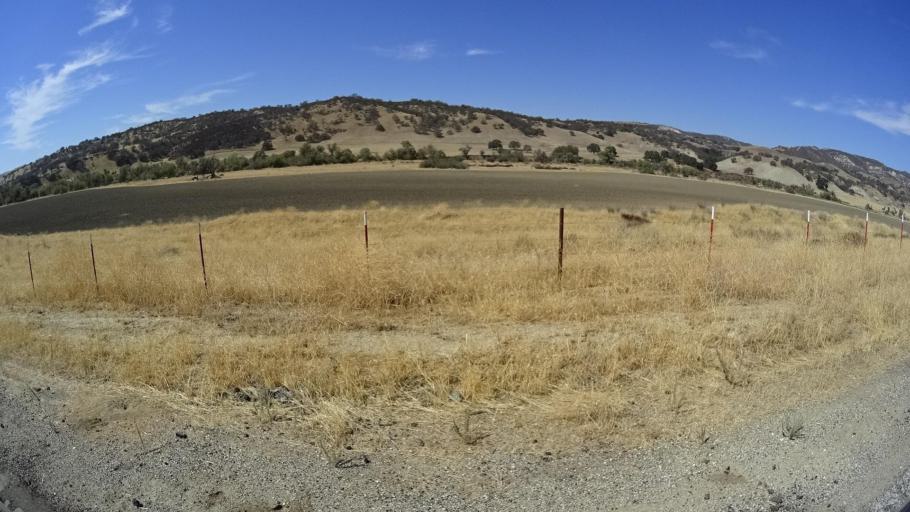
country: US
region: California
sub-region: San Luis Obispo County
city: San Miguel
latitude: 35.9262
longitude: -120.6794
